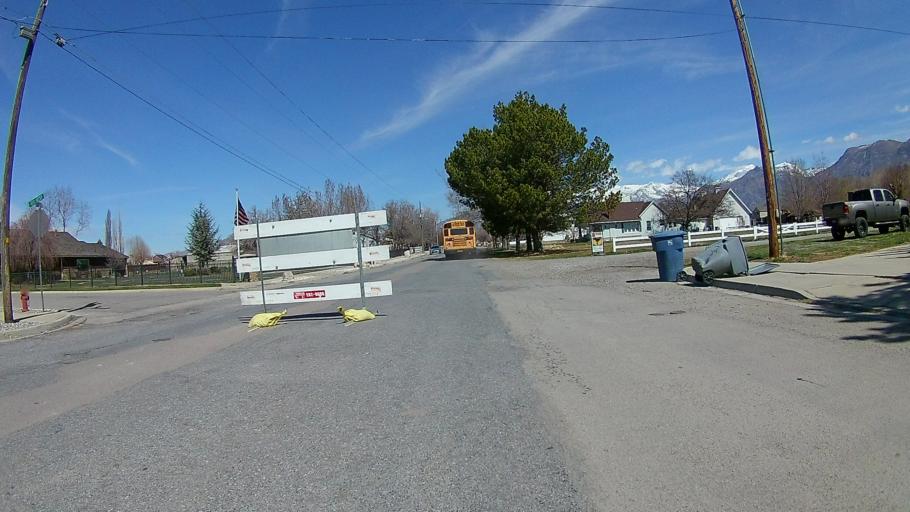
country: US
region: Utah
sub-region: Utah County
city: American Fork
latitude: 40.3660
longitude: -111.8014
